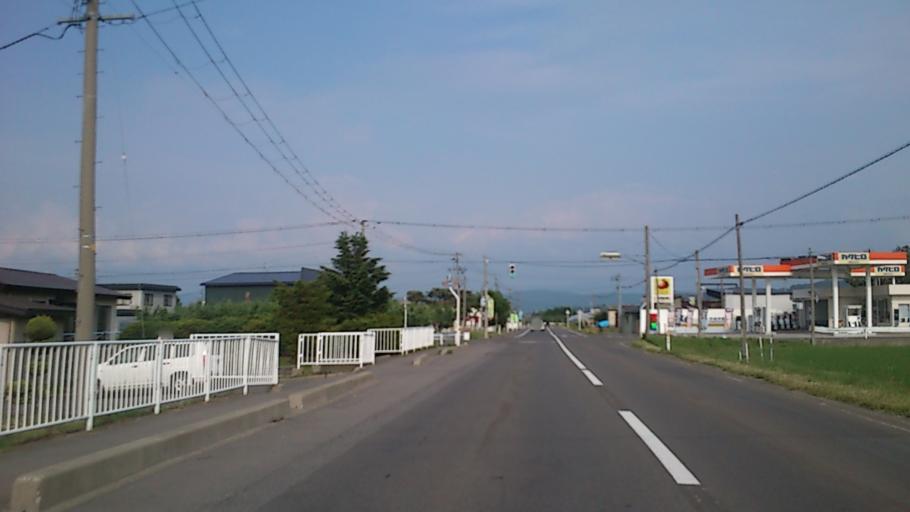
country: JP
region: Aomori
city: Hirosaki
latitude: 40.5596
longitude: 140.4963
